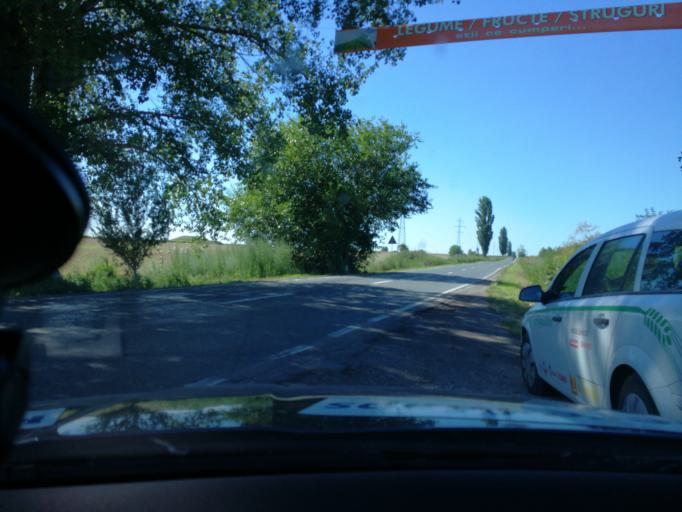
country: RO
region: Tulcea
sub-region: Comuna Greci
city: Greci
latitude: 45.1468
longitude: 28.2181
